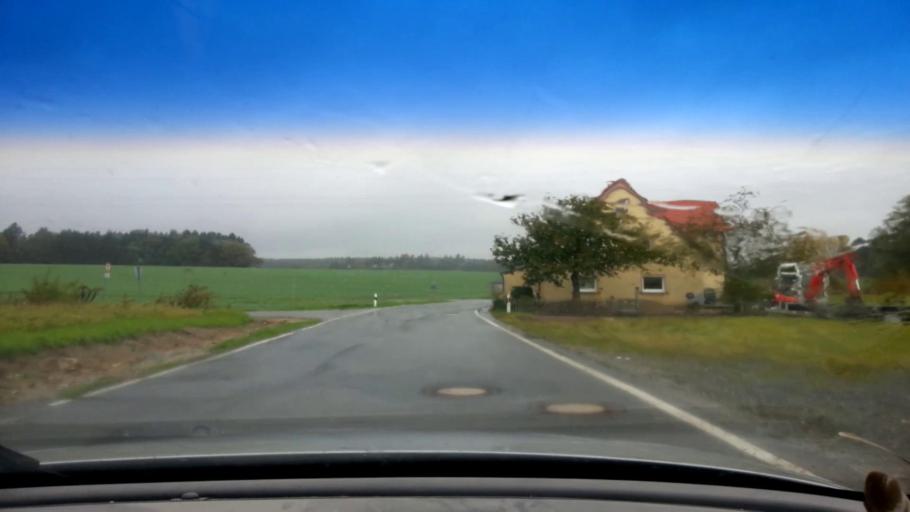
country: DE
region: Bavaria
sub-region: Upper Franconia
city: Stadelhofen
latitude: 50.0054
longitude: 11.1991
